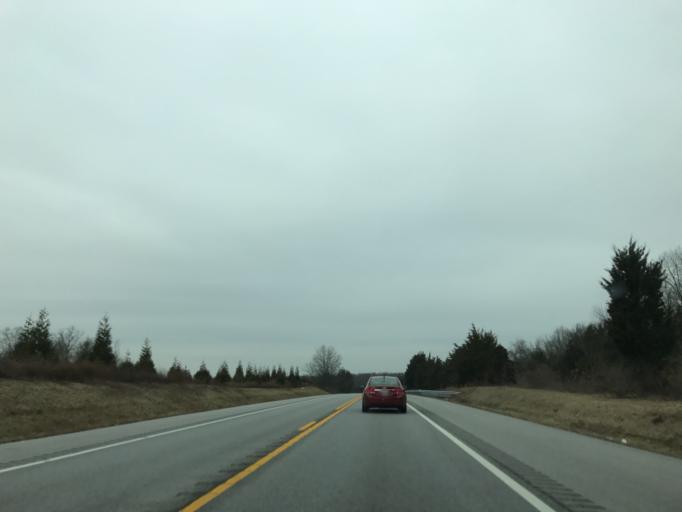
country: US
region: Maryland
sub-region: Carroll County
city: Taneytown
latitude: 39.6343
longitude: -77.1173
